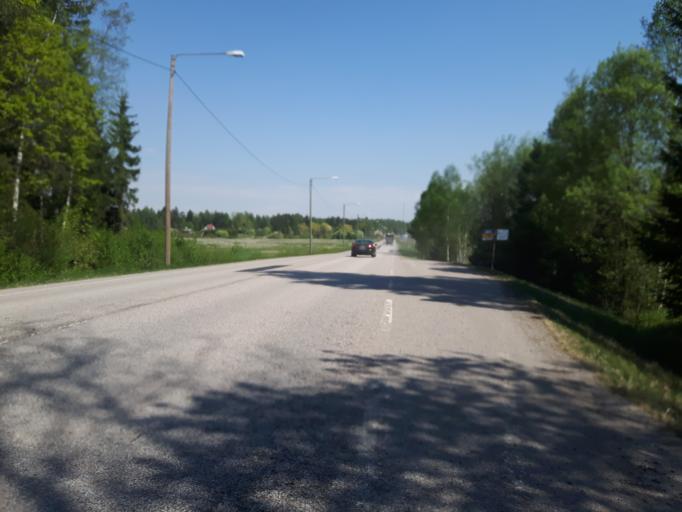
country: FI
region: Uusimaa
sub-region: Helsinki
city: Nickby
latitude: 60.3077
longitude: 25.3793
